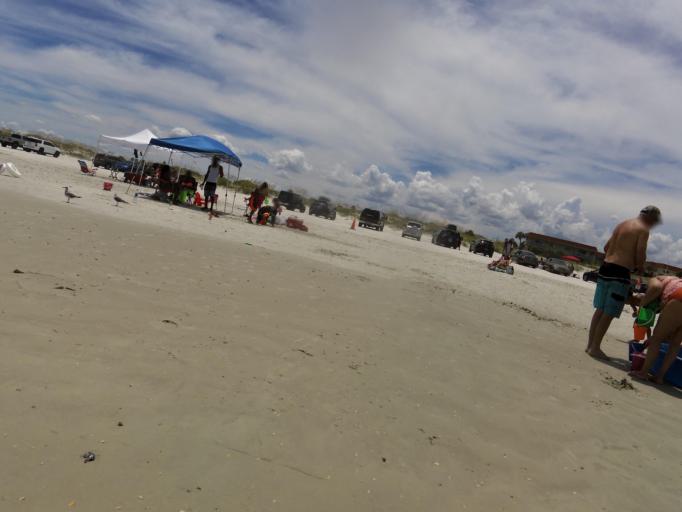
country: US
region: Florida
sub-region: Saint Johns County
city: Butler Beach
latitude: 29.8210
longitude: -81.2621
